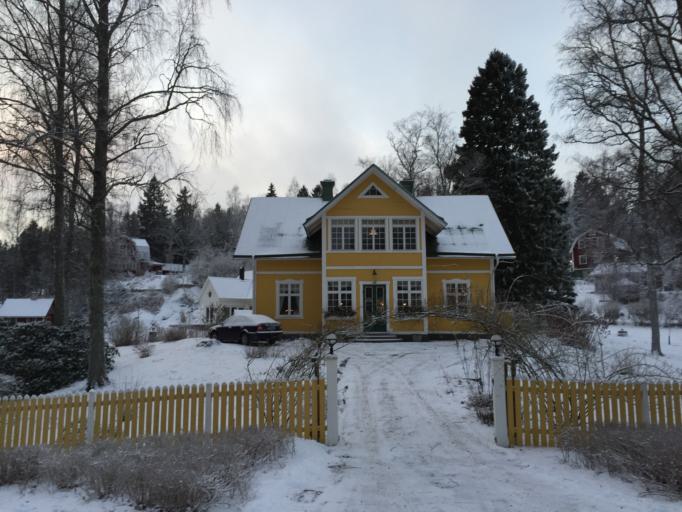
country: SE
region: Stockholm
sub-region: Salems Kommun
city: Ronninge
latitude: 59.1892
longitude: 17.7599
